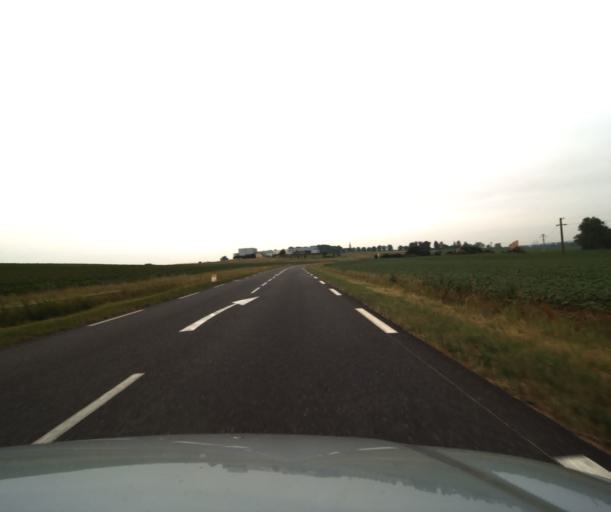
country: FR
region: Midi-Pyrenees
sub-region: Departement du Gers
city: Aubiet
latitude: 43.6823
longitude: 0.8200
